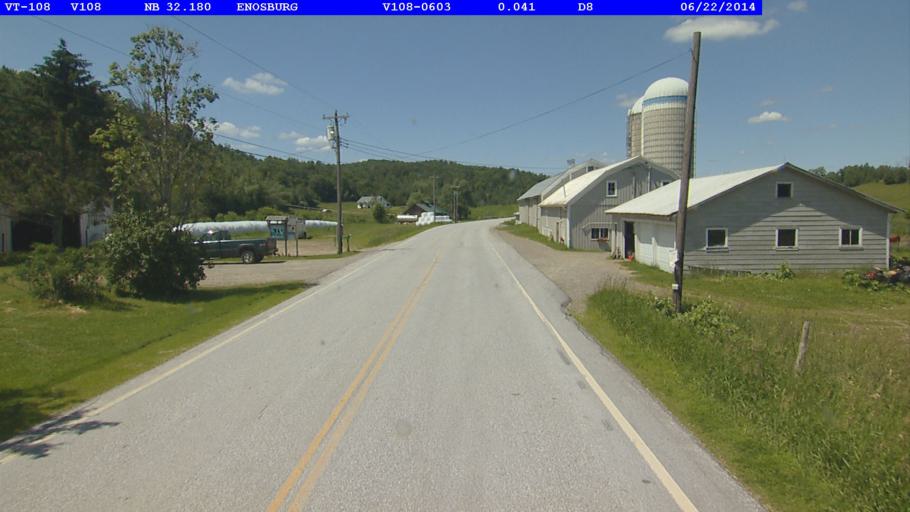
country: US
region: Vermont
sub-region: Franklin County
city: Enosburg Falls
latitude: 44.8390
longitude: -72.8055
